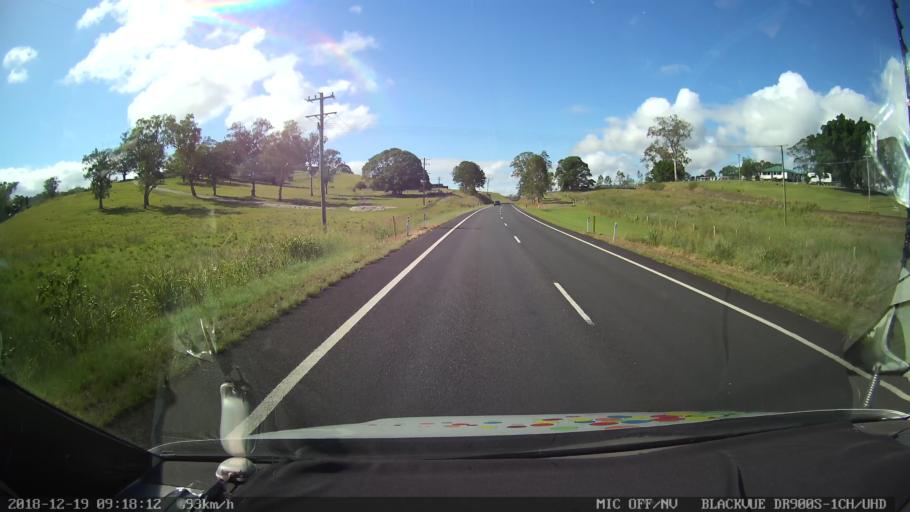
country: AU
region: New South Wales
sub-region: Kyogle
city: Kyogle
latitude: -28.5437
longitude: 152.9771
